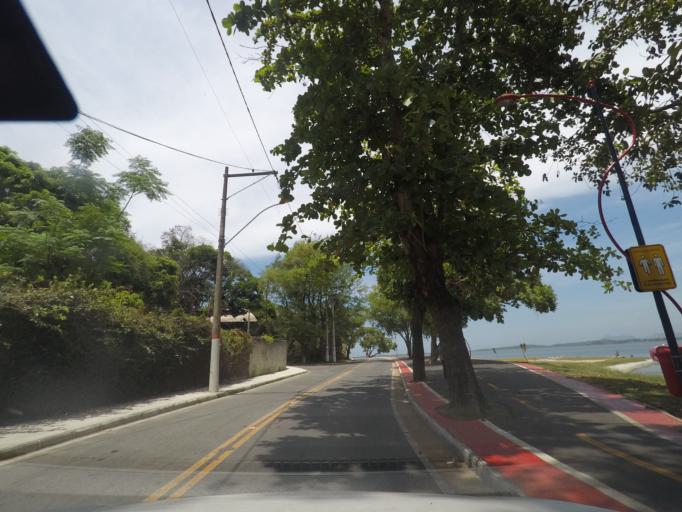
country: BR
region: Rio de Janeiro
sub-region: Marica
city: Marica
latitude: -22.9310
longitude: -42.8272
